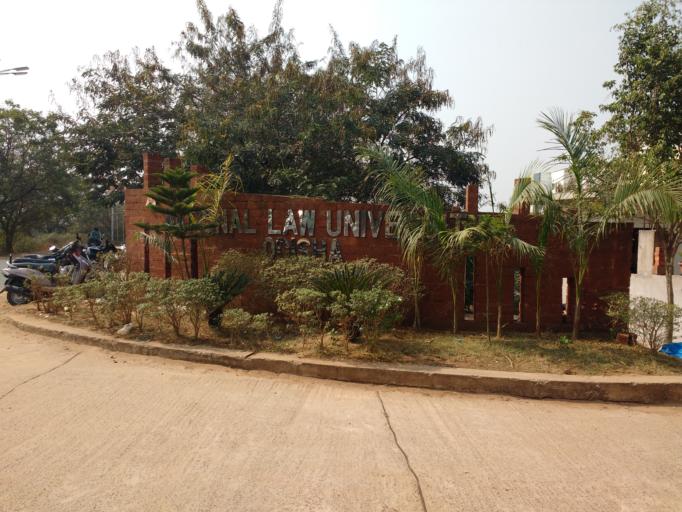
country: IN
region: Odisha
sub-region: Cuttack
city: Cuttack
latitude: 20.4842
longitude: 85.7903
